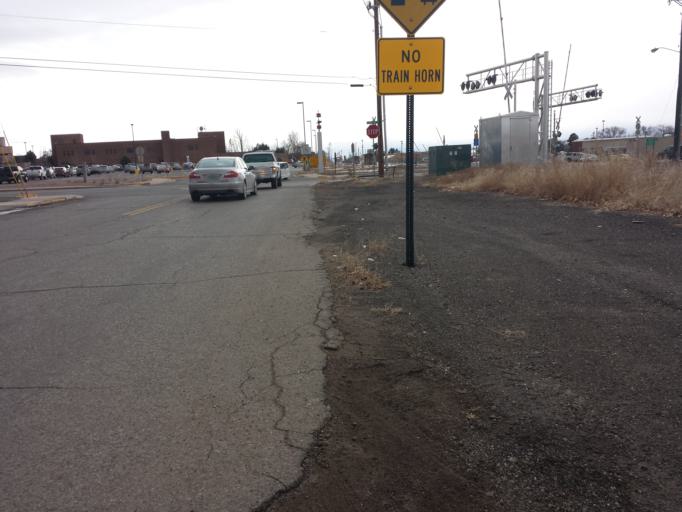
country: US
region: New Mexico
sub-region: Santa Fe County
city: Santa Fe
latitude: 35.6749
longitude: -105.9558
